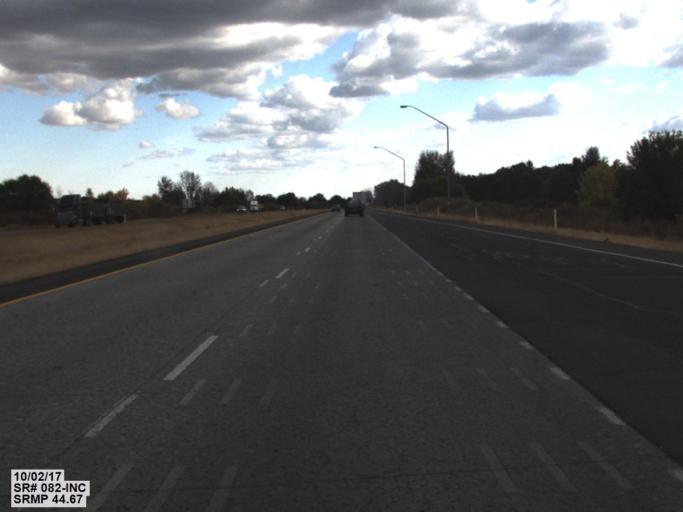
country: US
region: Washington
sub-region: Yakima County
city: Wapato
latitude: 46.4683
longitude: -120.3904
